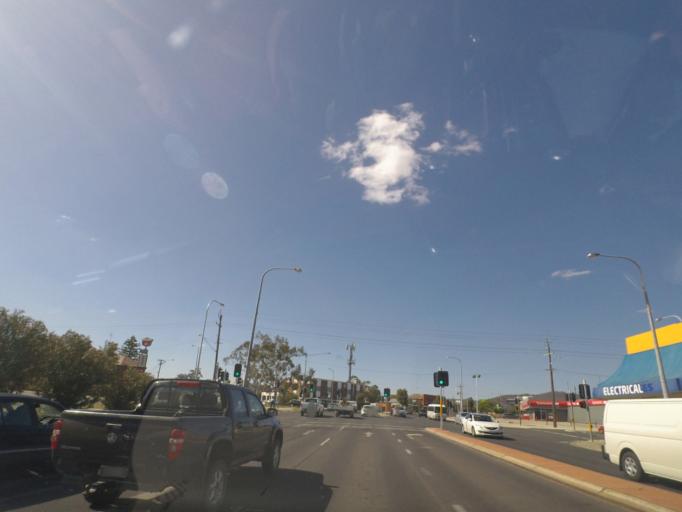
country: AU
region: New South Wales
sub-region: Albury Municipality
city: Lavington
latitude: -36.0529
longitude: 146.9335
